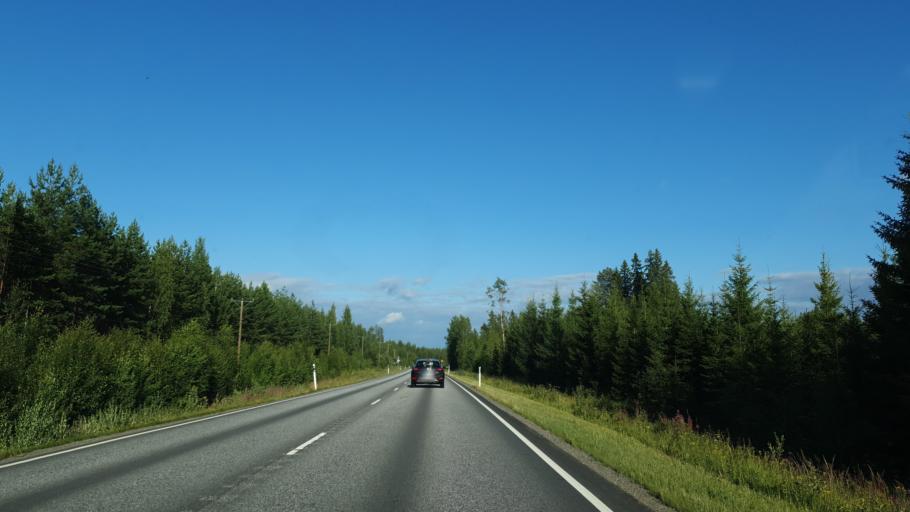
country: FI
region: North Karelia
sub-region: Joensuu
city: Outokumpu
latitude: 62.5328
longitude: 28.9643
